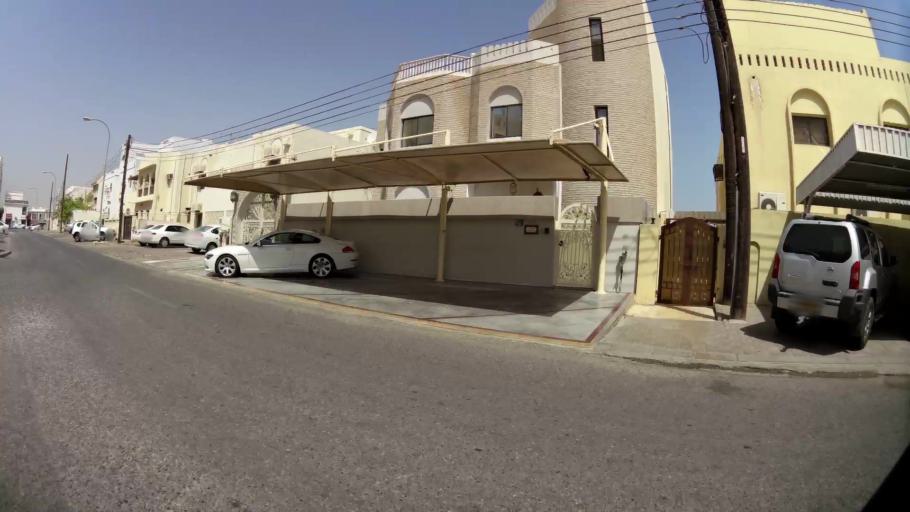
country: OM
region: Muhafazat Masqat
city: Bawshar
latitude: 23.5881
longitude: 58.4228
